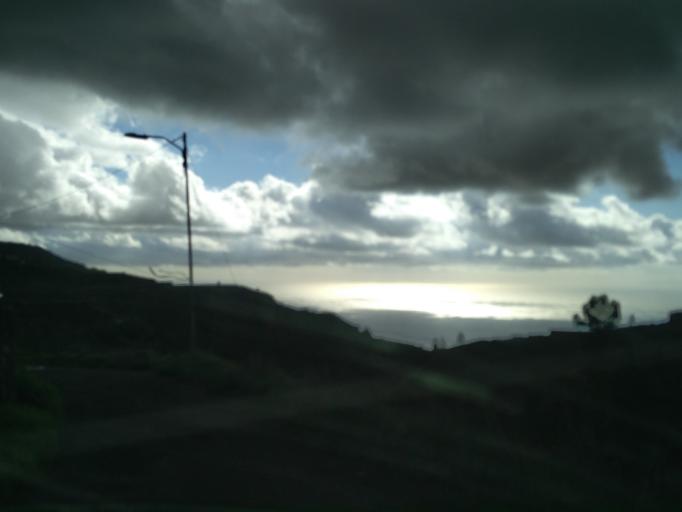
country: ES
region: Canary Islands
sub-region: Provincia de Santa Cruz de Tenerife
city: Arona
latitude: 28.1332
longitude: -16.6911
